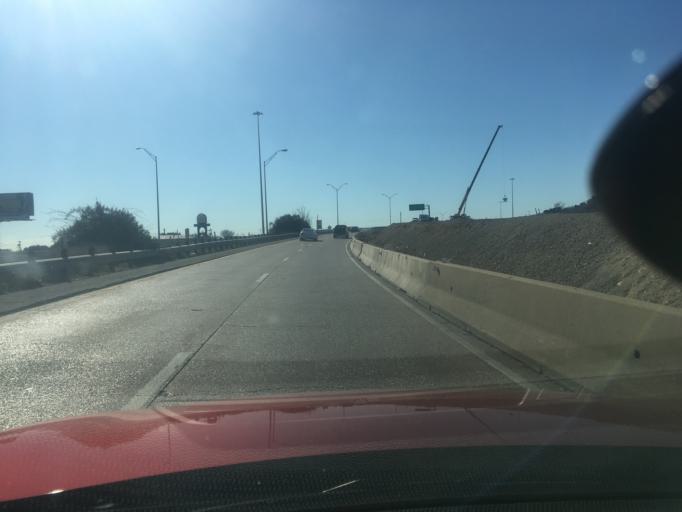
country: US
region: Texas
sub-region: Dallas County
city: Cockrell Hill
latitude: 32.7073
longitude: -96.8306
